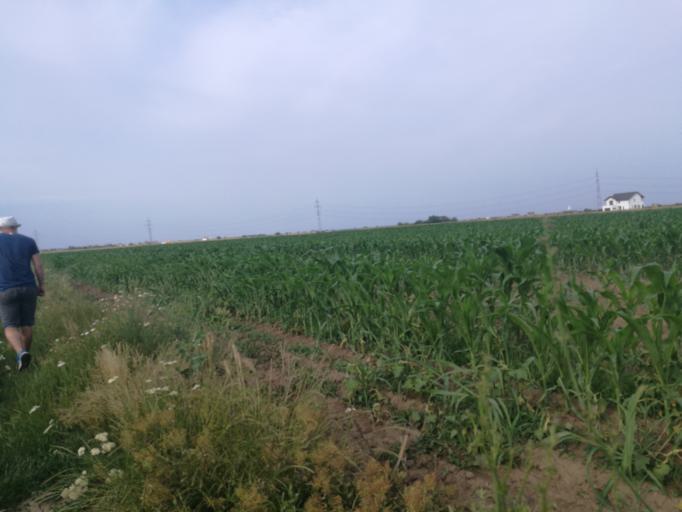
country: RO
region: Ilfov
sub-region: Comuna Vidra
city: Vidra
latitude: 44.2801
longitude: 26.1854
